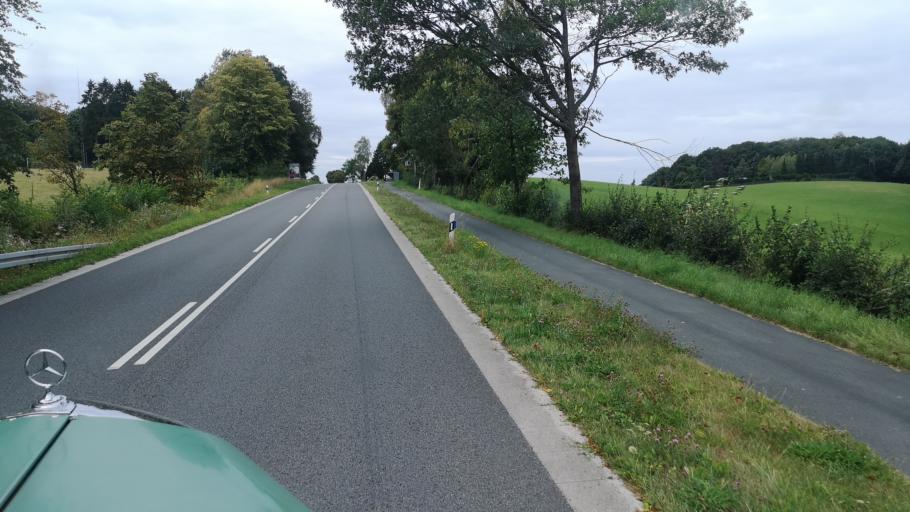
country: DE
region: North Rhine-Westphalia
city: Huckeswagen
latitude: 51.1001
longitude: 7.3384
